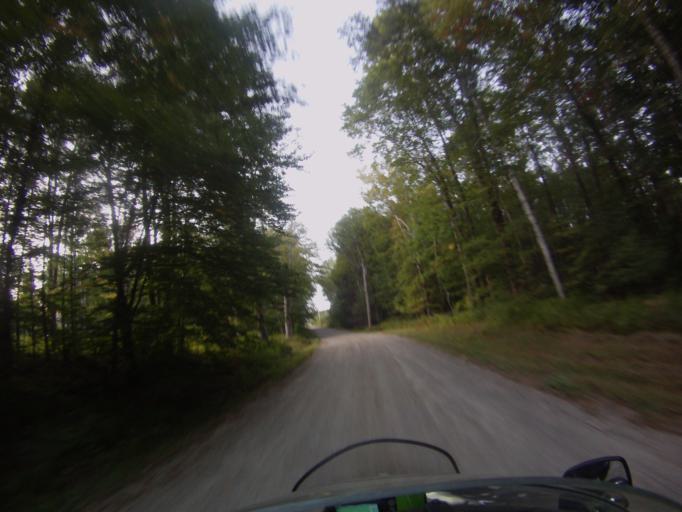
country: US
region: Vermont
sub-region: Addison County
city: Middlebury (village)
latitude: 43.9966
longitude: -73.0444
